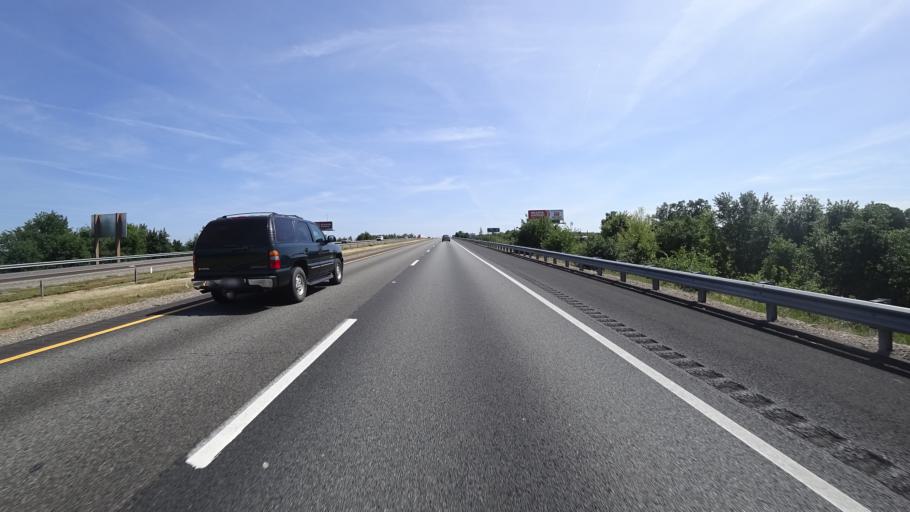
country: US
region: California
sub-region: Shasta County
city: Anderson
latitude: 40.4460
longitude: -122.2891
